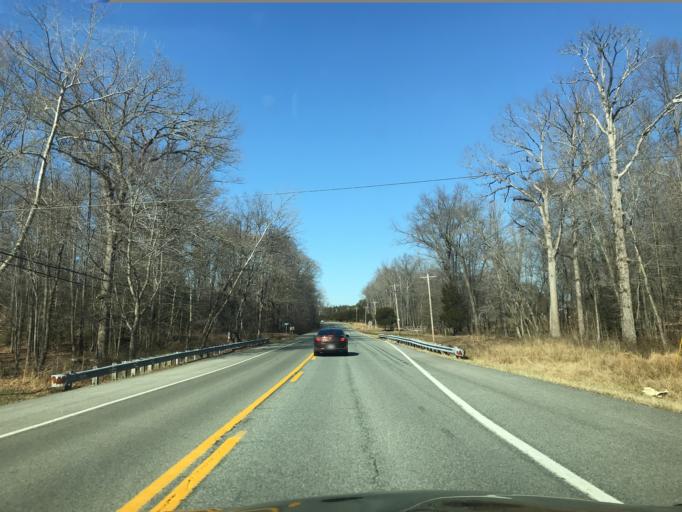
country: US
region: Maryland
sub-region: Charles County
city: Bryans Road
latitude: 38.6581
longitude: -77.0783
